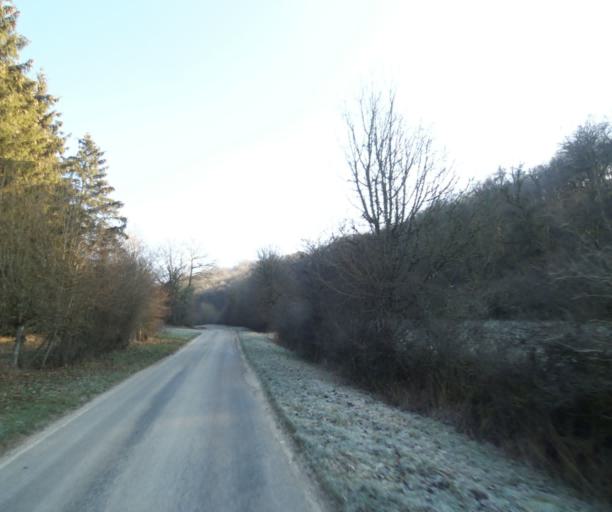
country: FR
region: Champagne-Ardenne
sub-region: Departement de la Haute-Marne
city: Joinville
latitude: 48.4909
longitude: 5.2161
